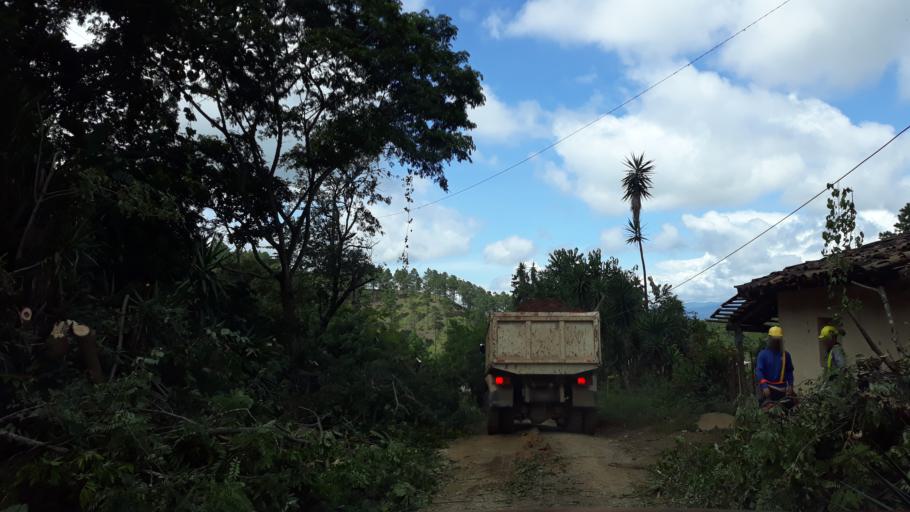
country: HN
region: El Paraiso
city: Santa Cruz
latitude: 13.7549
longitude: -86.6560
